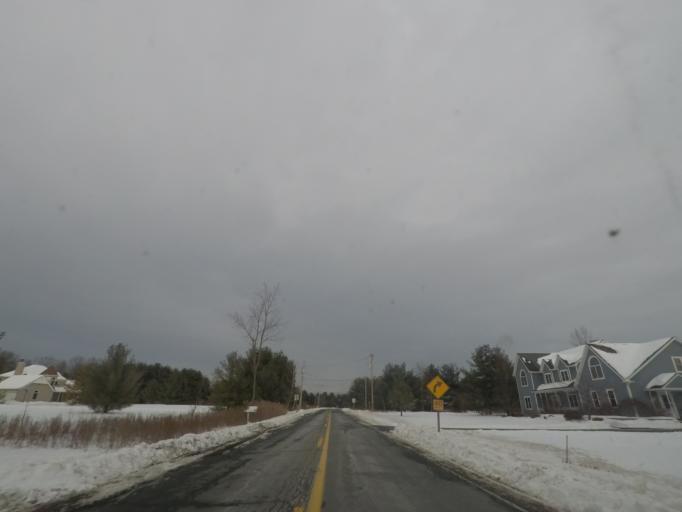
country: US
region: New York
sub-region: Rensselaer County
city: Castleton-on-Hudson
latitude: 42.5172
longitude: -73.7369
